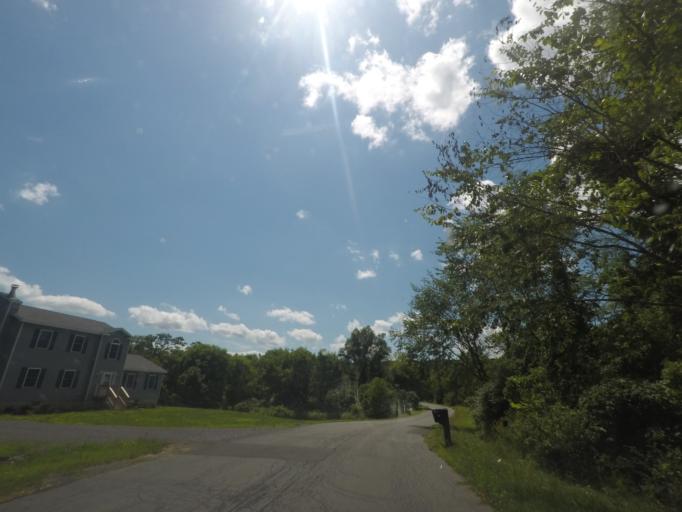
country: US
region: New York
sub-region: Albany County
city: Voorheesville
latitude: 42.7168
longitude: -73.9524
